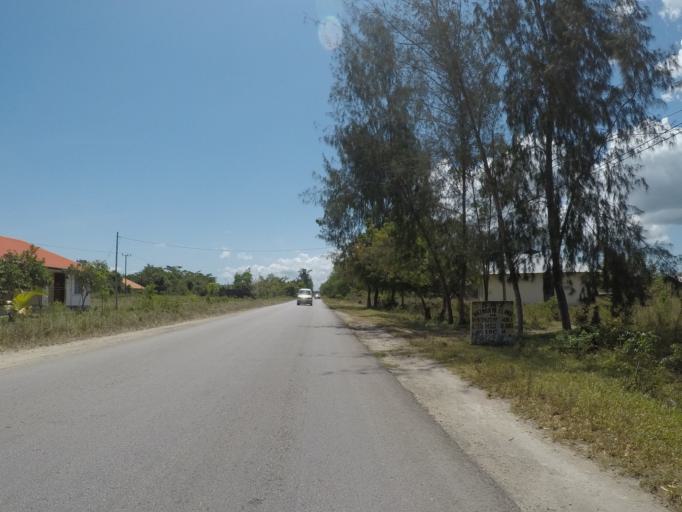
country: TZ
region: Zanzibar Central/South
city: Nganane
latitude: -6.2821
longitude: 39.4347
